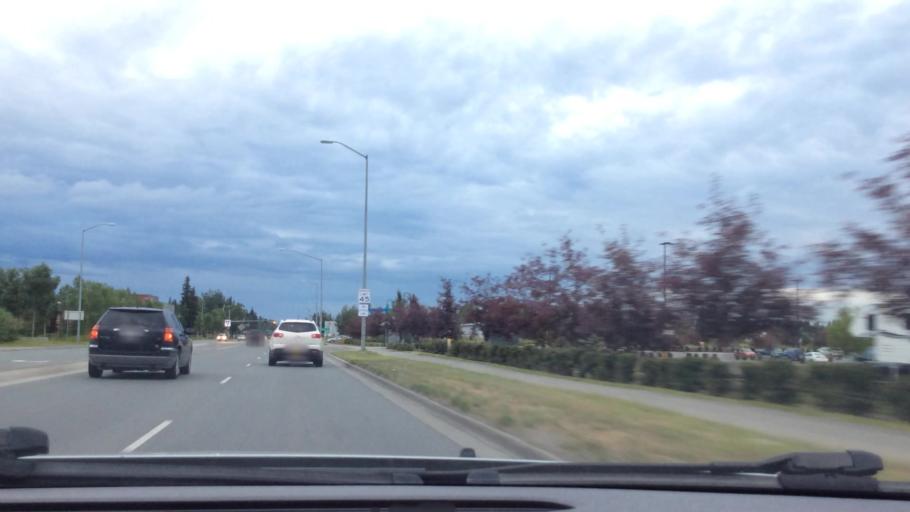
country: US
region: Alaska
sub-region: Anchorage Municipality
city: Elmendorf Air Force Base
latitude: 61.2098
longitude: -149.7420
